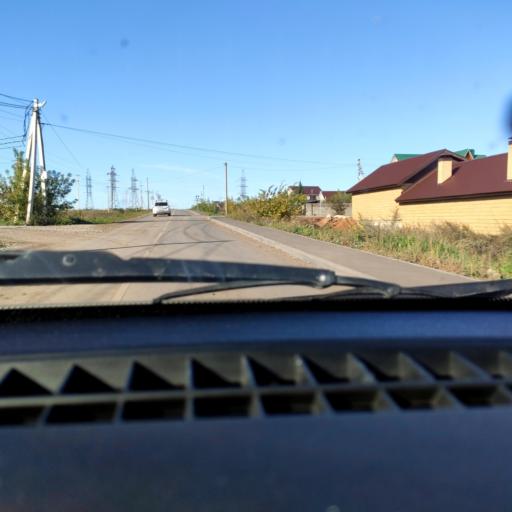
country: RU
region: Bashkortostan
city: Avdon
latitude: 54.6049
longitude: 55.7836
